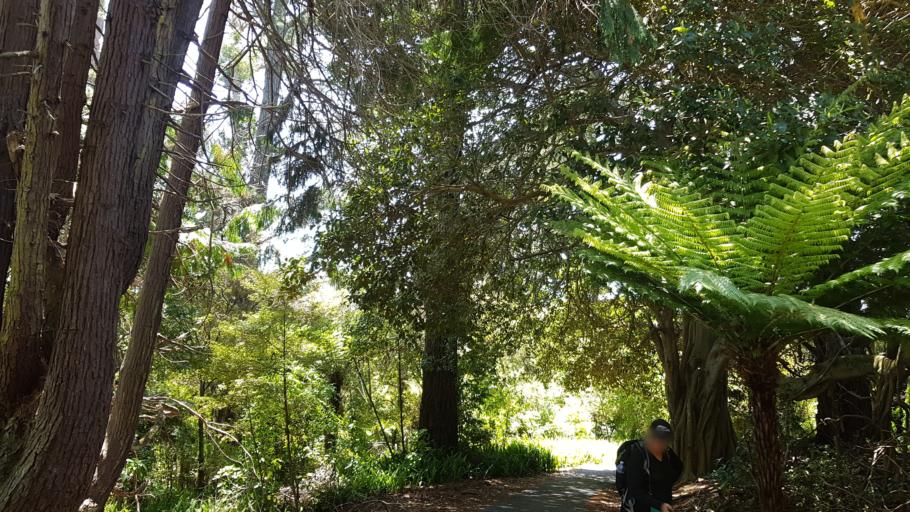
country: NZ
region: Auckland
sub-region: Auckland
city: North Shore
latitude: -36.8213
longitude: 174.7192
